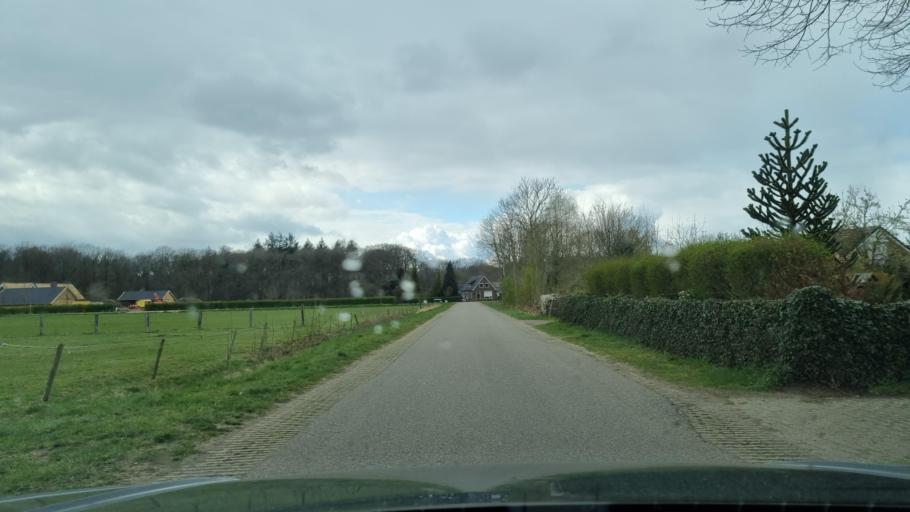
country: NL
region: Gelderland
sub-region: Gemeente Montferland
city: s-Heerenberg
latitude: 51.8995
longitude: 6.1776
